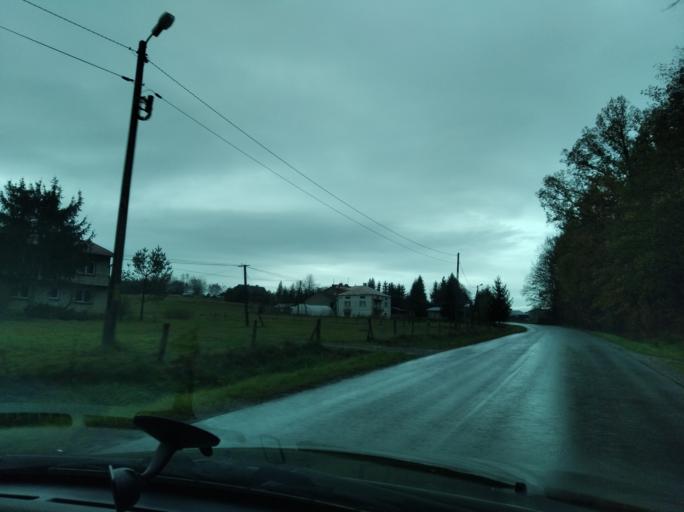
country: PL
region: Subcarpathian Voivodeship
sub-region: Powiat rzeszowski
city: Lecka
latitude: 49.9067
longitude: 22.0215
